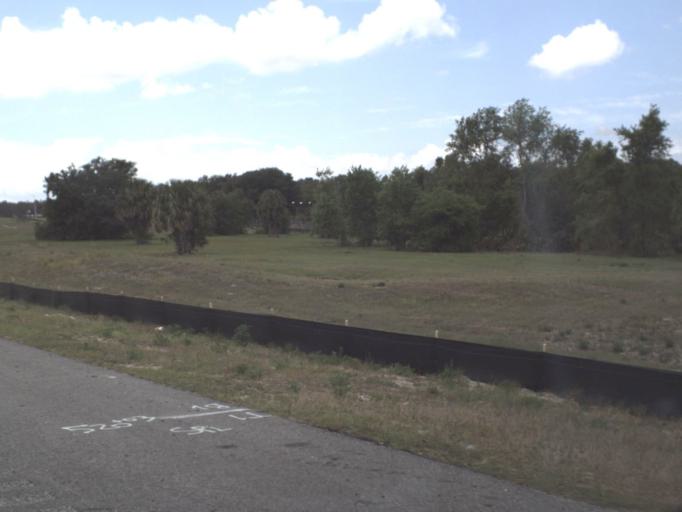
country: US
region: Florida
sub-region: Lake County
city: Mount Plymouth
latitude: 28.7832
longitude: -81.5217
